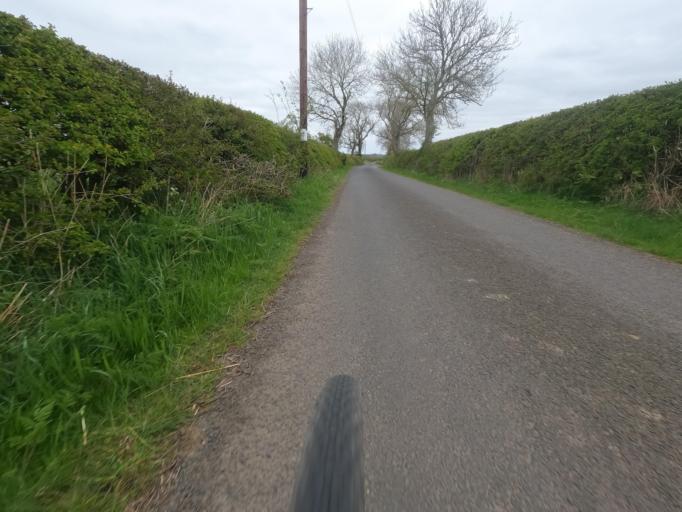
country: GB
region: England
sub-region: Northumberland
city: Meldon
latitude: 55.0767
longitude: -1.8091
